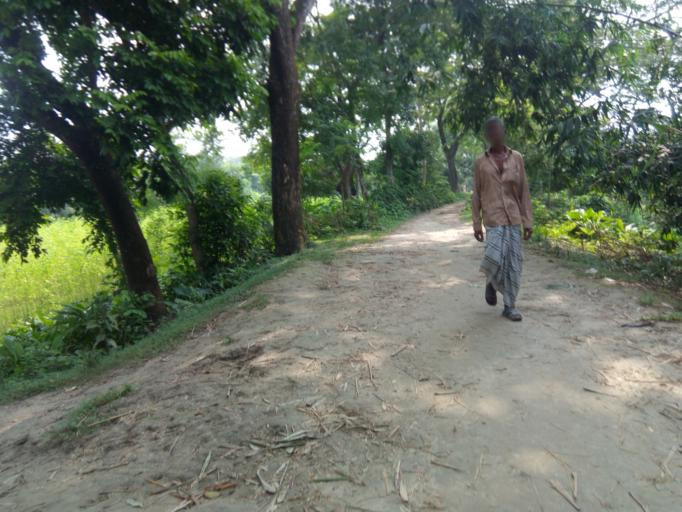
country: BD
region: Khulna
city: Kalia
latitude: 23.0592
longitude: 89.6564
